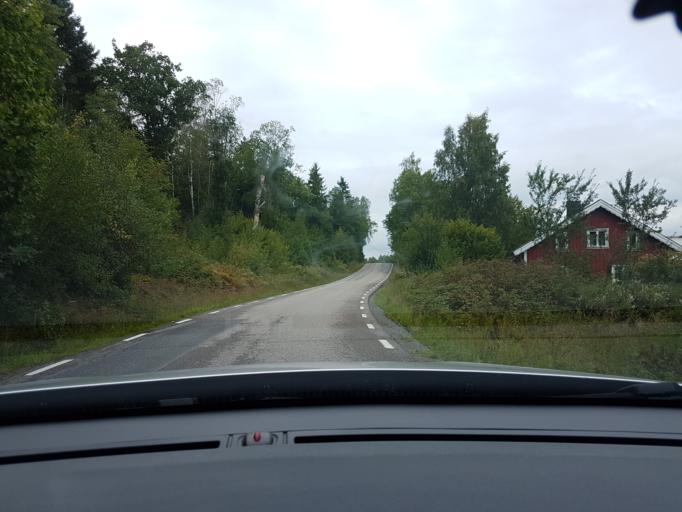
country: SE
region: Vaestra Goetaland
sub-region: Ale Kommun
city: Alvangen
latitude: 57.9189
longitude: 12.1333
